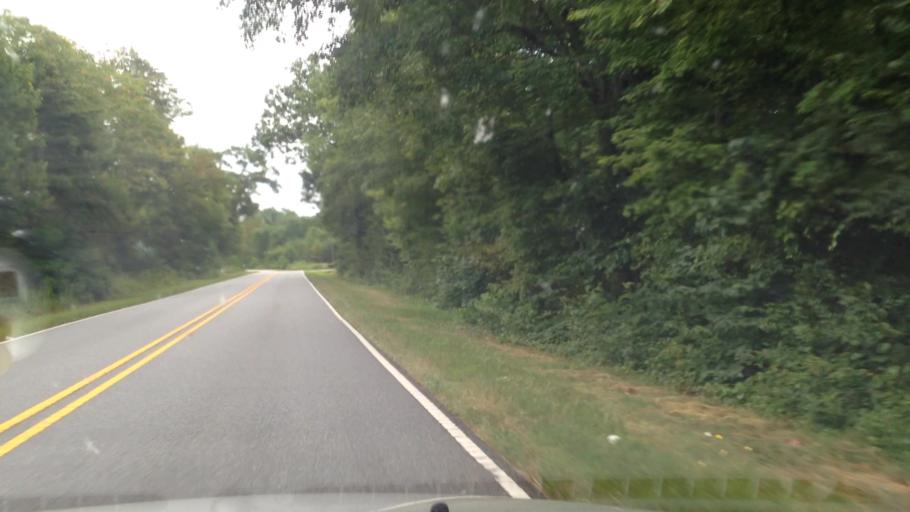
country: US
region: North Carolina
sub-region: Rockingham County
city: Mayodan
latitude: 36.4203
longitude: -80.0812
